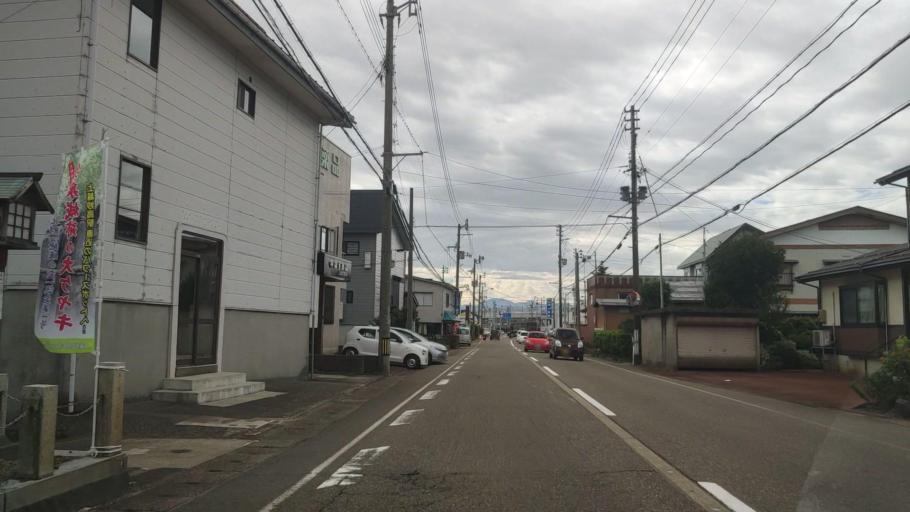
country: JP
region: Niigata
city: Joetsu
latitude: 37.0848
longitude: 138.2500
